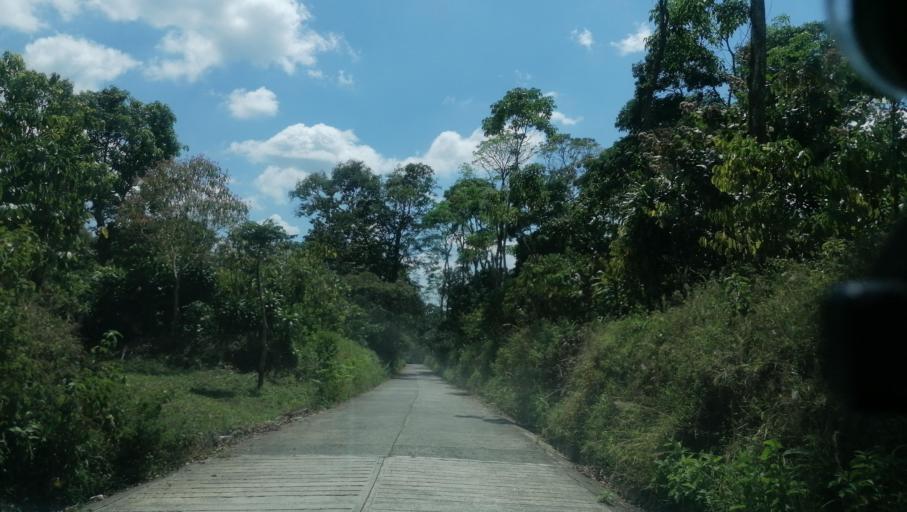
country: MX
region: Chiapas
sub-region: Union Juarez
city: Santo Domingo
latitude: 15.0388
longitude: -92.1440
